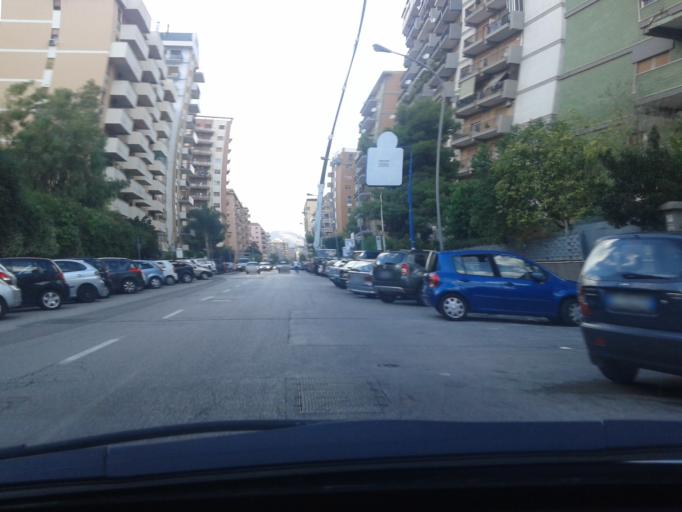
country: IT
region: Sicily
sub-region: Palermo
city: Palermo
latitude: 38.1490
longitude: 13.3298
